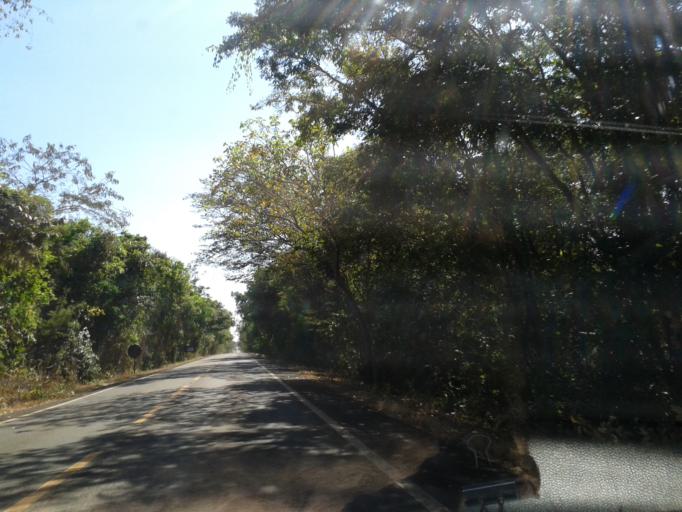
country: BR
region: Goias
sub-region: Crixas
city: Crixas
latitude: -13.9611
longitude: -50.3204
